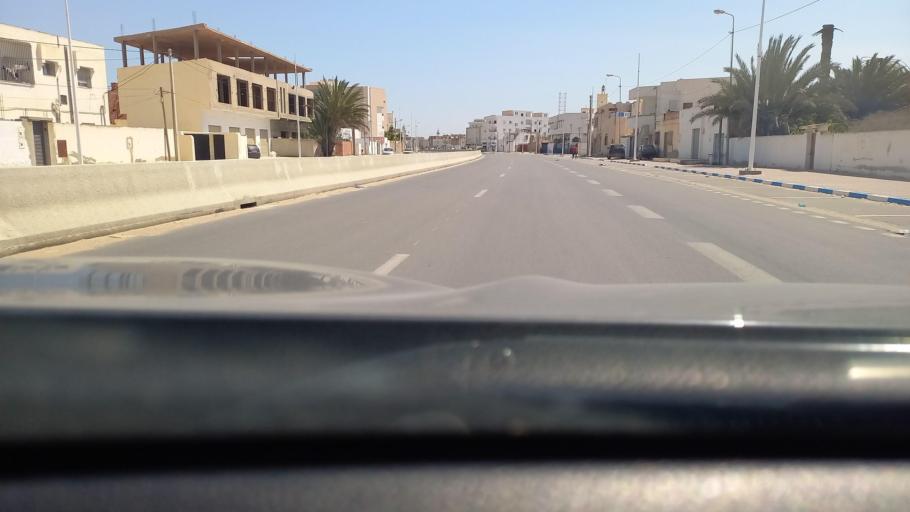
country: TN
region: Safaqis
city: Sfax
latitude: 34.7426
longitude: 10.7244
